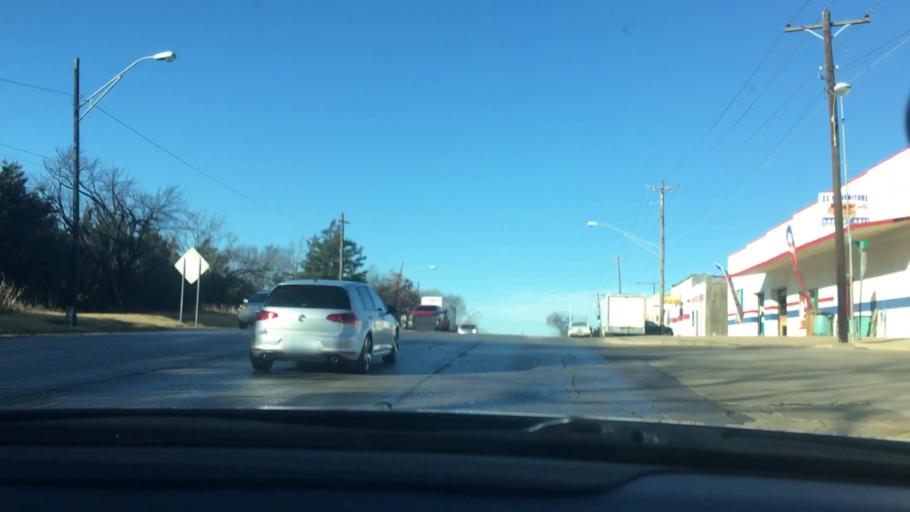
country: US
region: Oklahoma
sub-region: Murray County
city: Sulphur
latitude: 34.5065
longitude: -96.9699
